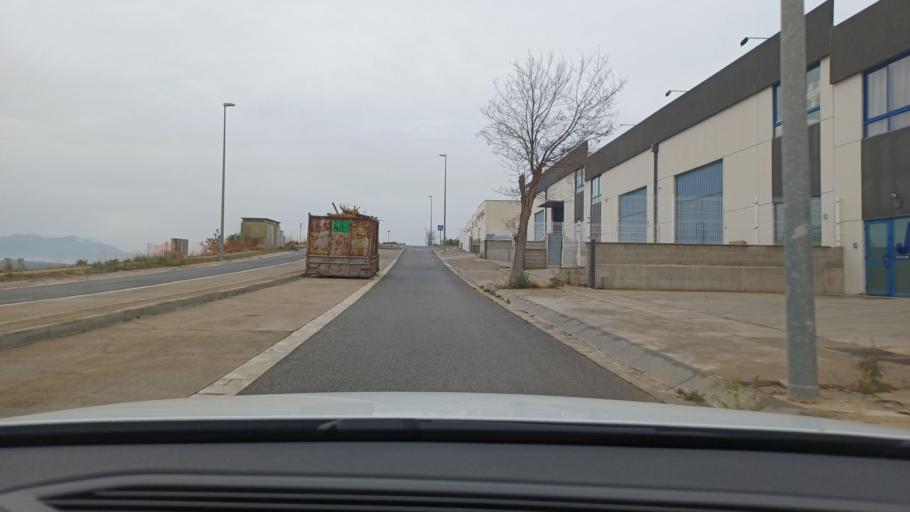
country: ES
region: Catalonia
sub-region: Provincia de Tarragona
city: Amposta
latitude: 40.7667
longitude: 0.5944
